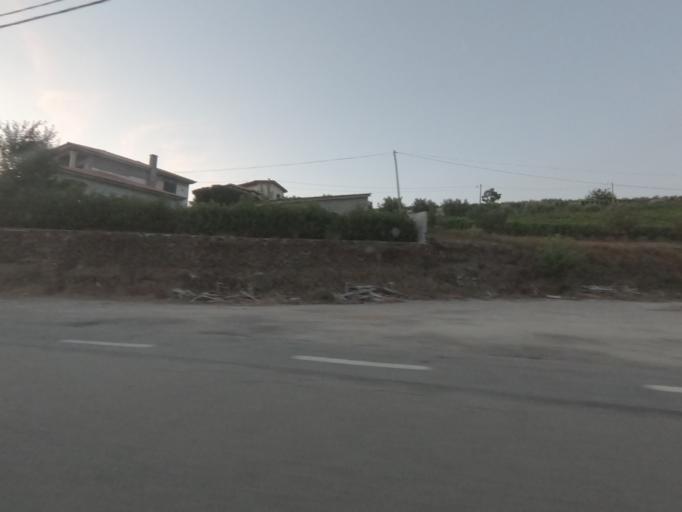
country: PT
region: Vila Real
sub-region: Peso da Regua
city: Peso da Regua
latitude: 41.2023
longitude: -7.7003
